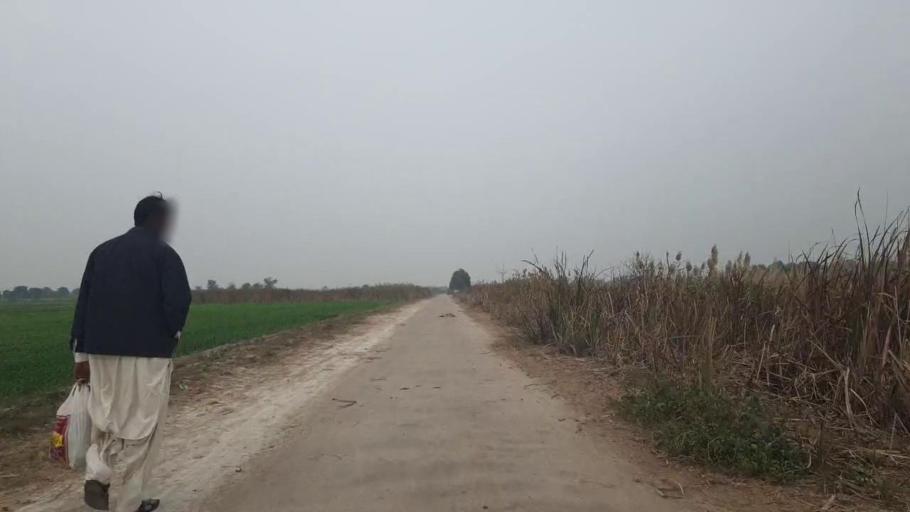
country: PK
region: Sindh
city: Tando Adam
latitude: 25.8380
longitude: 68.6574
